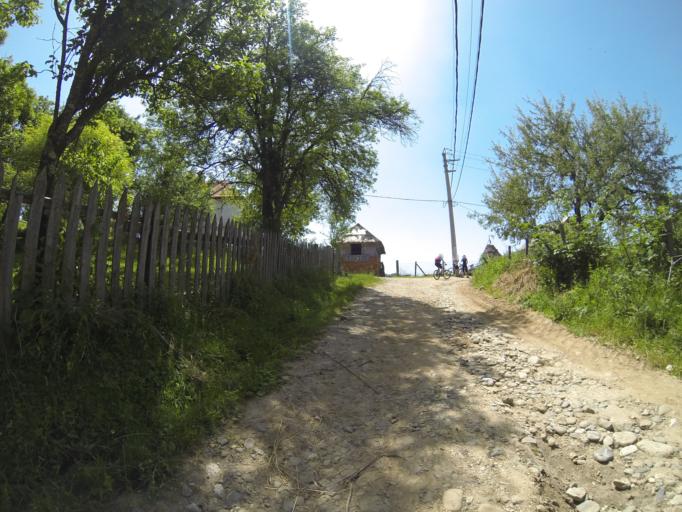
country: RO
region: Valcea
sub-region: Oras Baile Olanesti
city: Baile Olanesti
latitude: 45.2049
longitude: 24.2164
